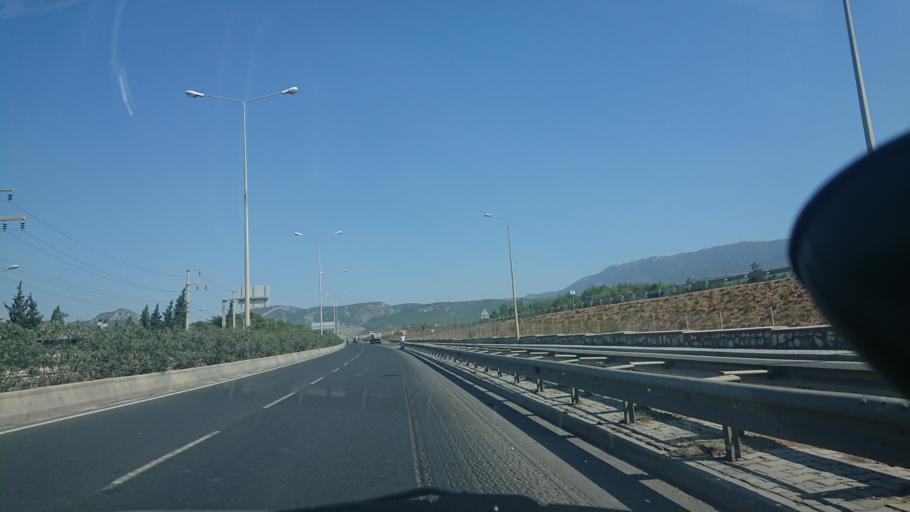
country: TR
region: Izmir
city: Bornova
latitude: 38.4516
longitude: 27.2691
